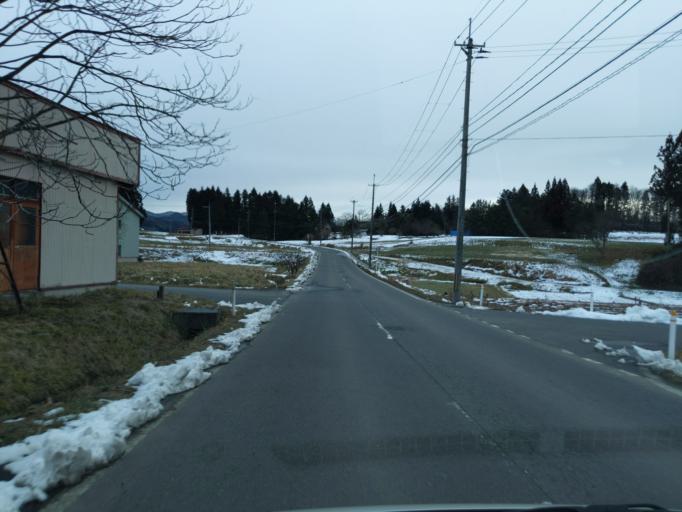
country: JP
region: Iwate
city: Mizusawa
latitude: 39.1820
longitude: 141.2449
